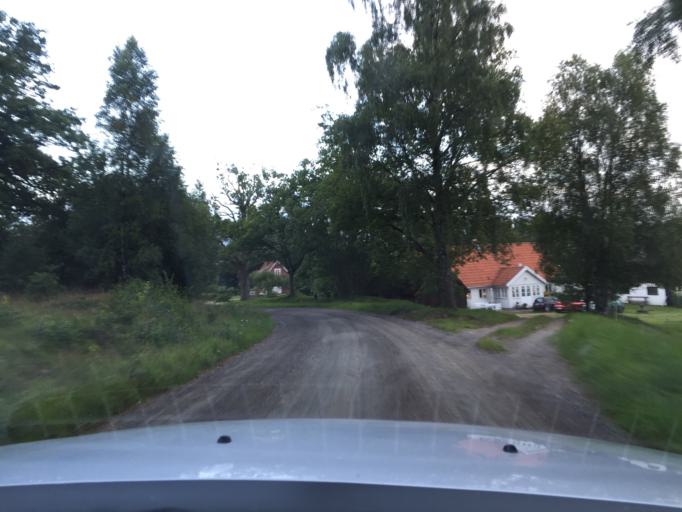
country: SE
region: Skane
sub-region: Hassleholms Kommun
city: Sosdala
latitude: 56.0621
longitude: 13.6611
